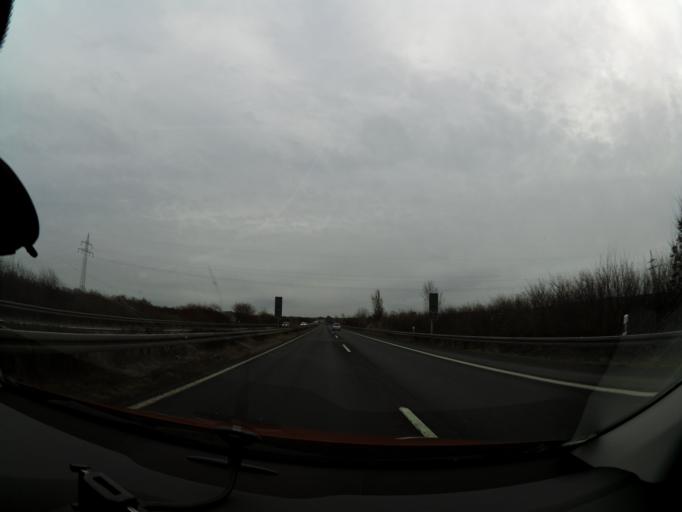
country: DE
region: Lower Saxony
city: Schladen
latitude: 52.0151
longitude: 10.5324
